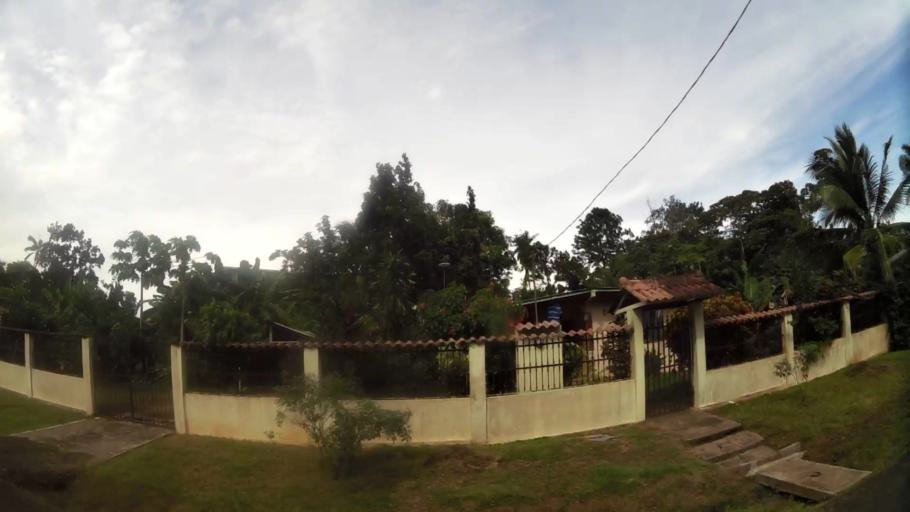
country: PA
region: Panama
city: El Coco
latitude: 8.8661
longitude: -79.8068
